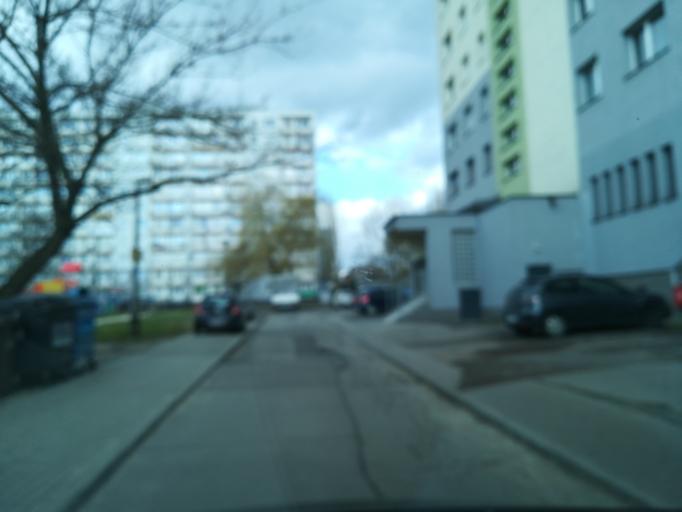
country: PL
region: Silesian Voivodeship
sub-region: Sosnowiec
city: Sosnowiec
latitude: 50.2936
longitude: 19.1320
